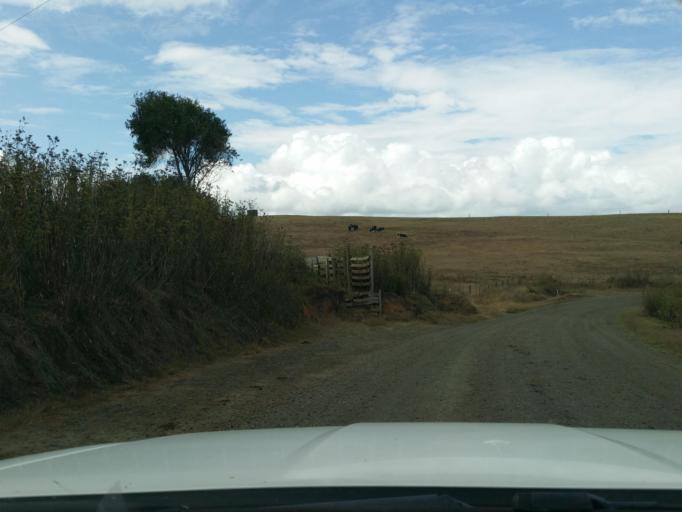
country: NZ
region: Auckland
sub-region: Auckland
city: Wellsford
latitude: -36.3306
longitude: 174.1551
